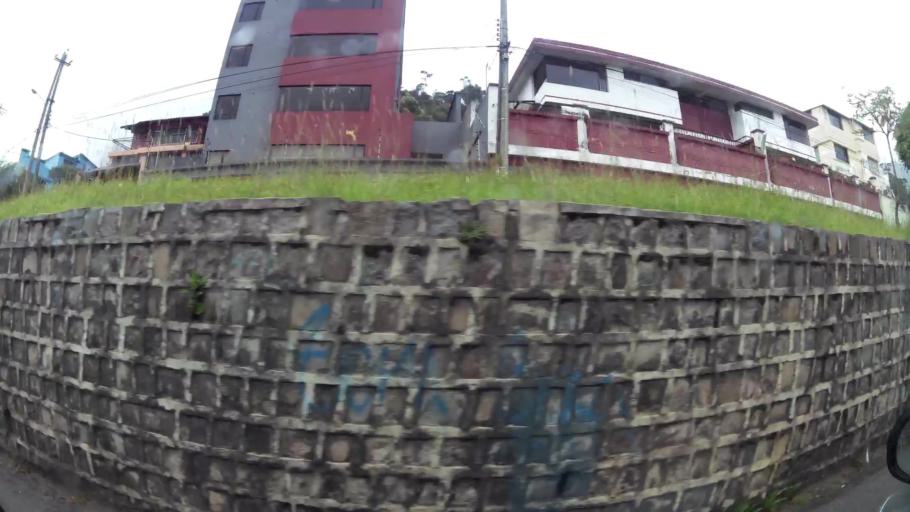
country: EC
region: Pichincha
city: Quito
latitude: -0.2032
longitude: -78.5101
